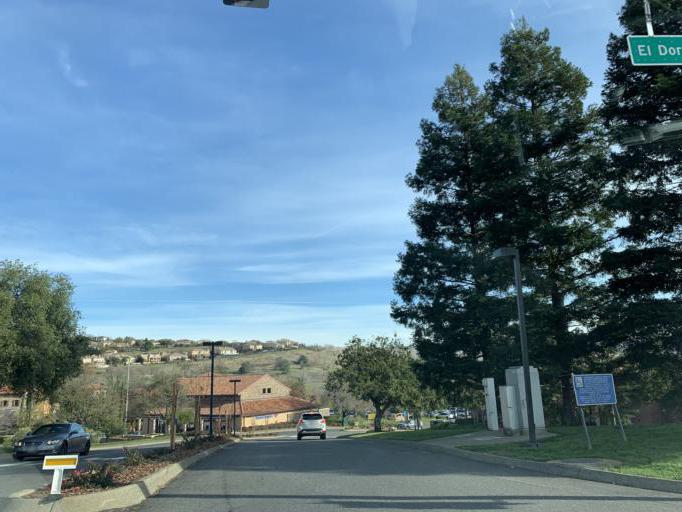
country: US
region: California
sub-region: El Dorado County
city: El Dorado Hills
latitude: 38.6568
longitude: -121.0717
